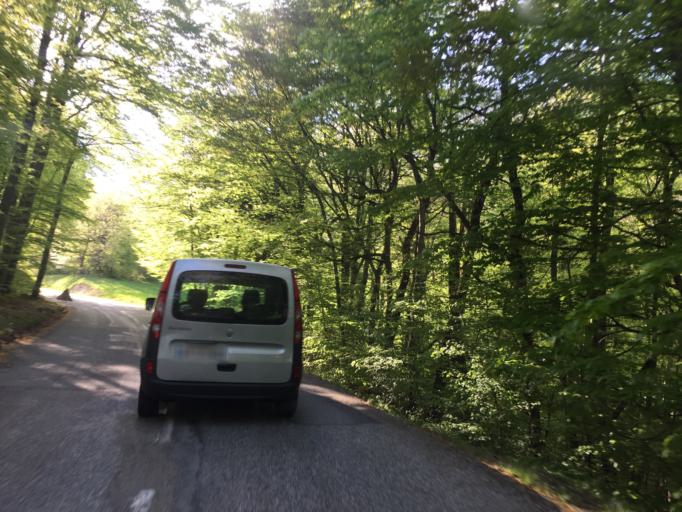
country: FR
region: Rhone-Alpes
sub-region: Departement de la Savoie
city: Frontenex
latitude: 45.6638
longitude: 6.3035
